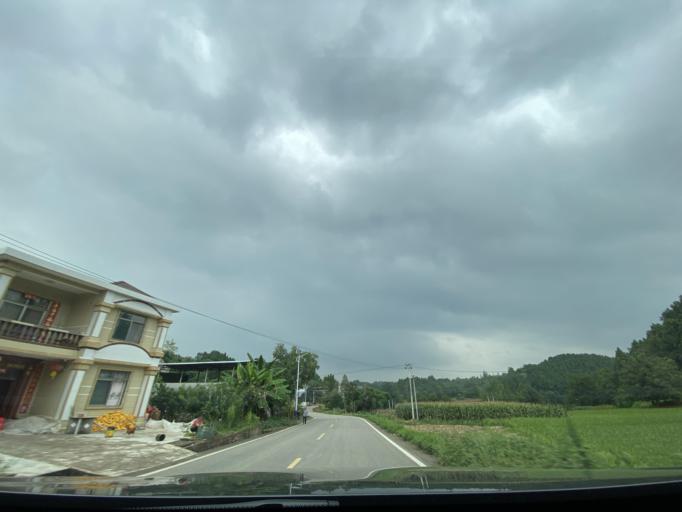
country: CN
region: Sichuan
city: Jiancheng
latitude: 30.5467
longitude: 104.5195
